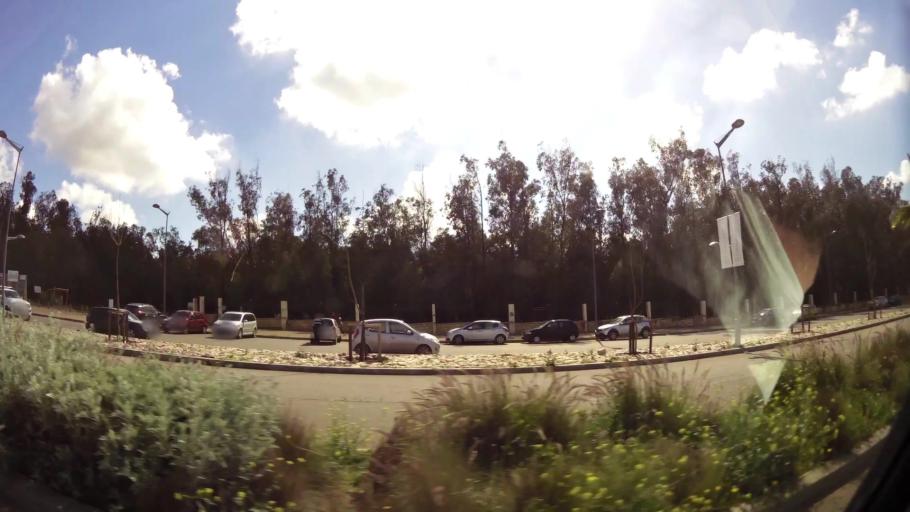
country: MA
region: Grand Casablanca
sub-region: Nouaceur
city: Bouskoura
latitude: 33.4731
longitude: -7.6162
